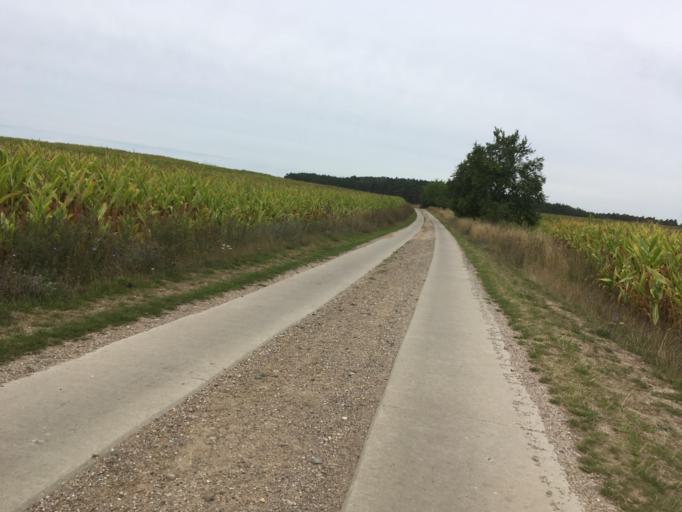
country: DE
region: Brandenburg
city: Gerswalde
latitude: 53.1845
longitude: 13.8367
